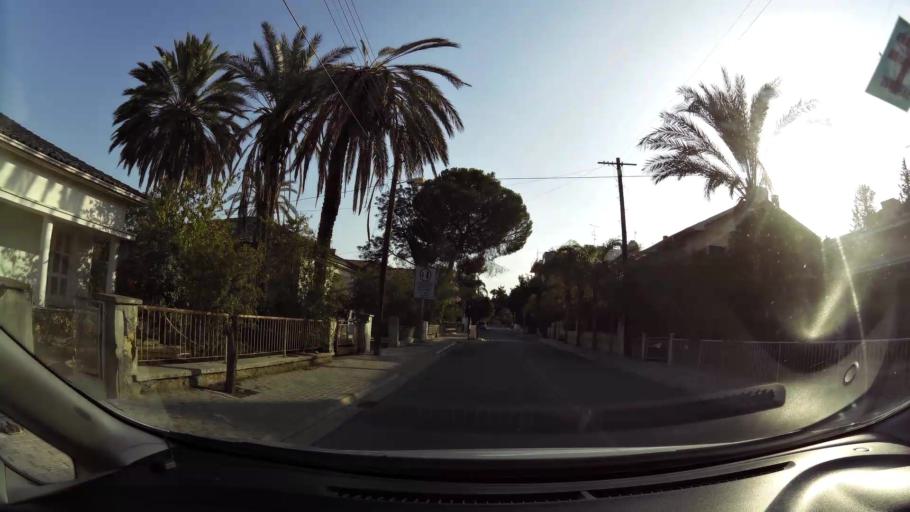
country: CY
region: Lefkosia
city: Nicosia
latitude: 35.1734
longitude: 33.3447
